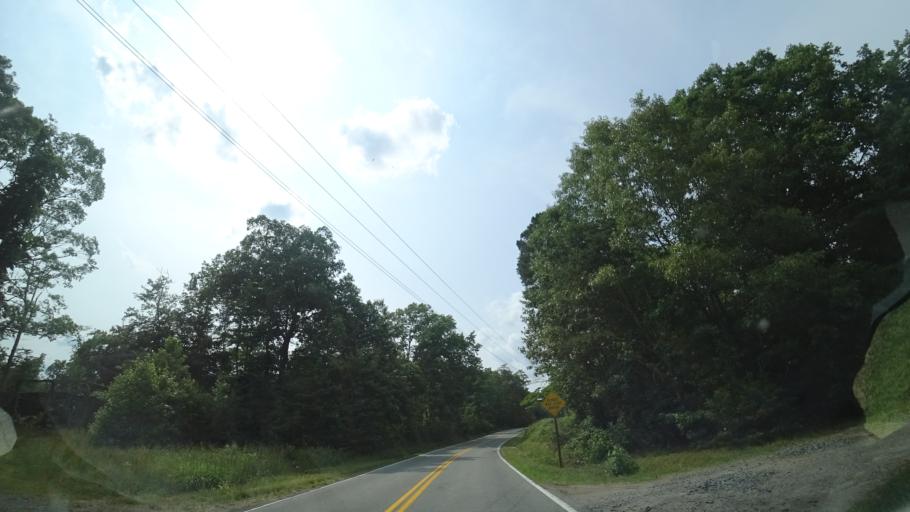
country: US
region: Virginia
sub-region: Spotsylvania County
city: Spotsylvania
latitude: 38.1247
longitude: -77.7755
